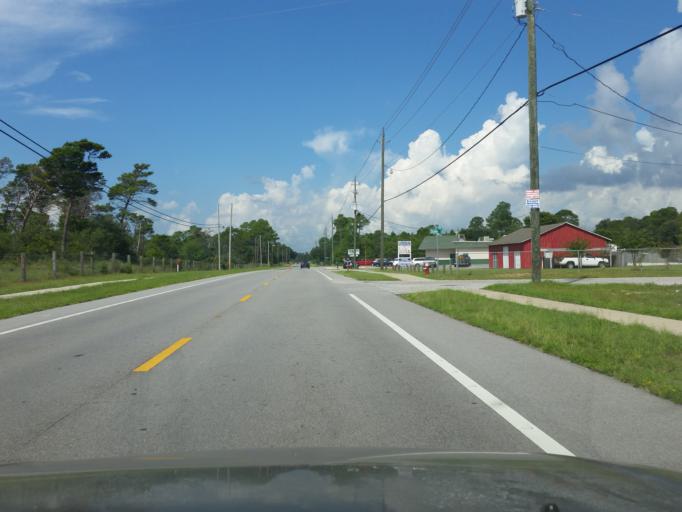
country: US
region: Florida
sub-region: Escambia County
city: Myrtle Grove
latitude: 30.3211
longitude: -87.4083
